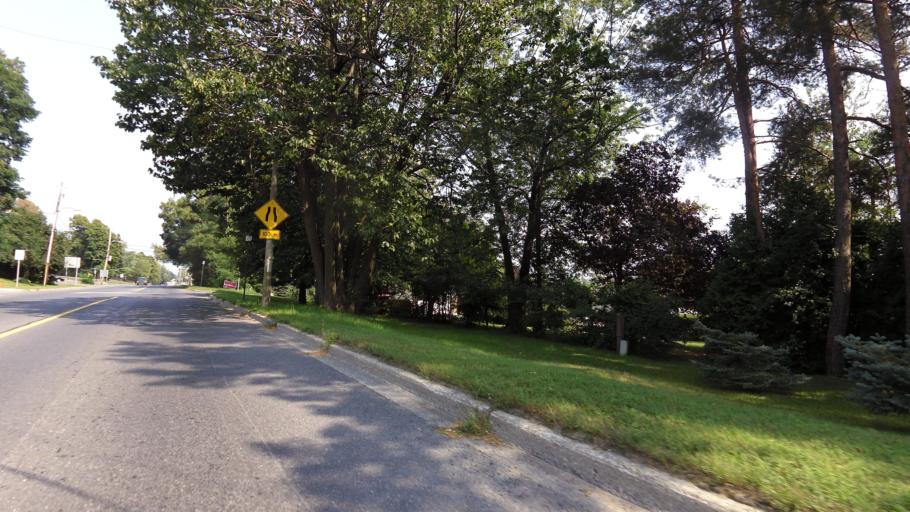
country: CA
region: Ontario
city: Brockville
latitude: 44.6004
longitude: -75.6678
